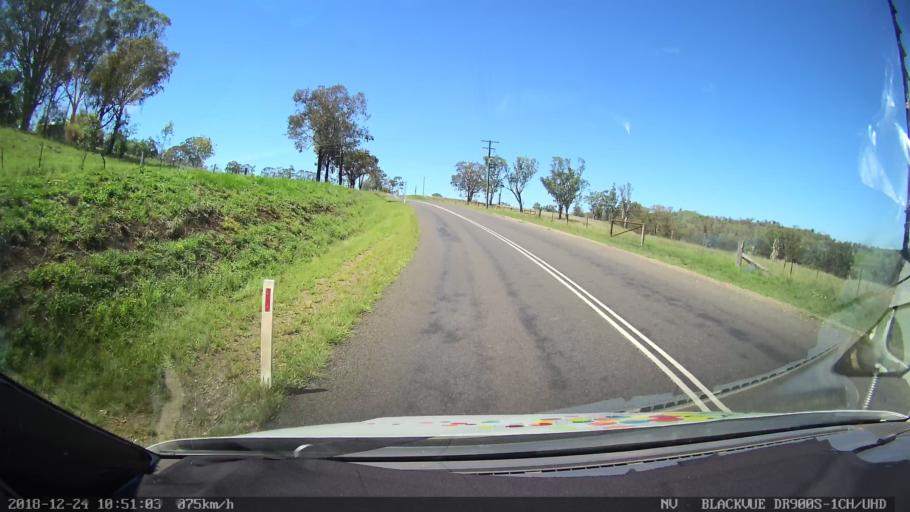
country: AU
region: New South Wales
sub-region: Upper Hunter Shire
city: Merriwa
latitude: -31.9655
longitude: 150.4228
